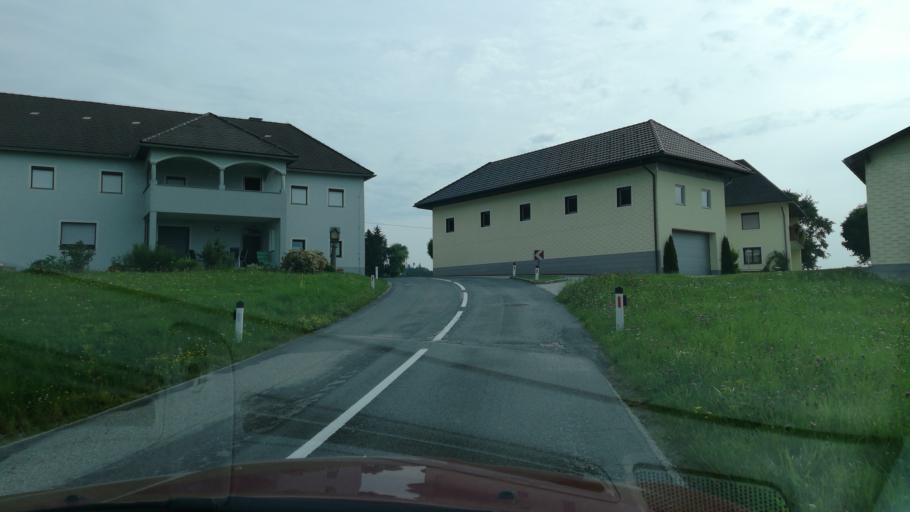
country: AT
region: Upper Austria
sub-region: Politischer Bezirk Rohrbach
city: Kleinzell im Muehlkreis
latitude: 48.4922
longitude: 14.0210
